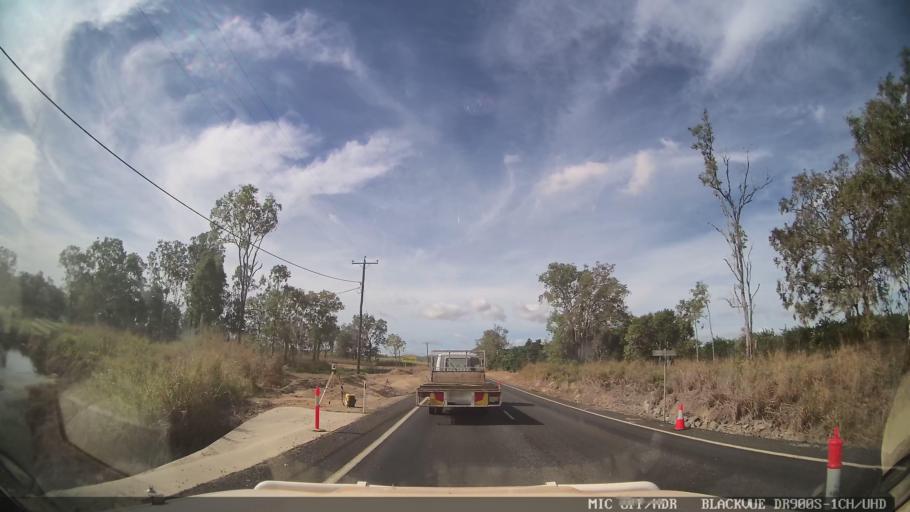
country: AU
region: Queensland
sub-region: Tablelands
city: Mareeba
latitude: -16.9920
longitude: 145.4694
